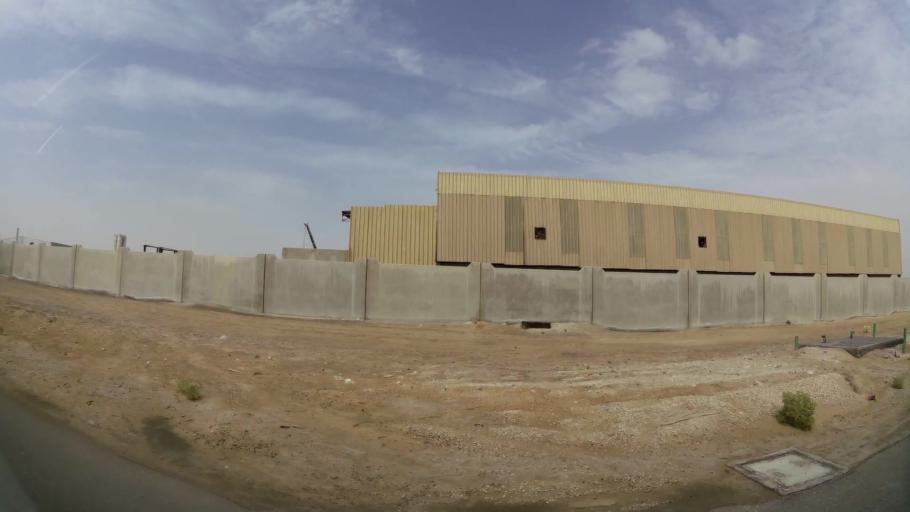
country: AE
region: Abu Dhabi
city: Abu Dhabi
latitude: 24.3295
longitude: 54.5024
